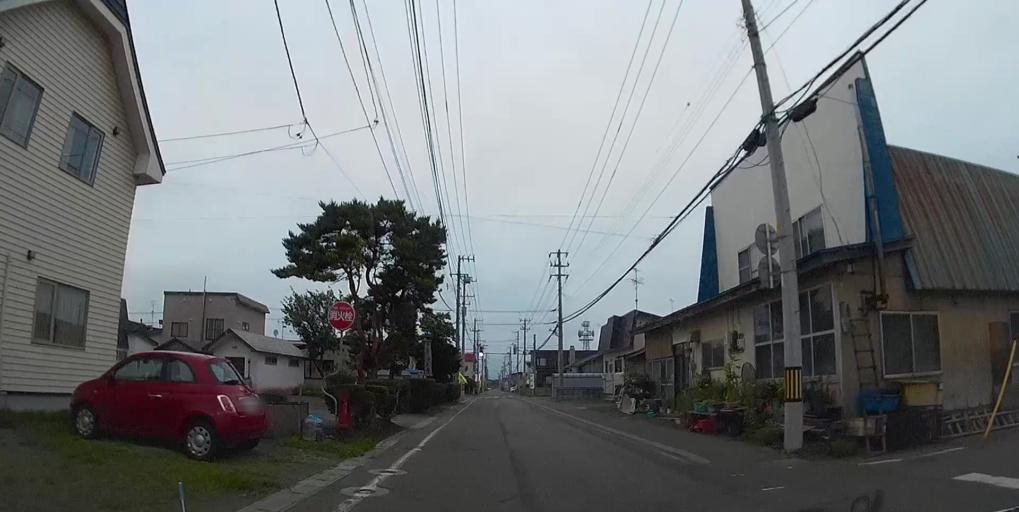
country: JP
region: Hokkaido
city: Nanae
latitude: 42.2581
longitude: 140.2695
